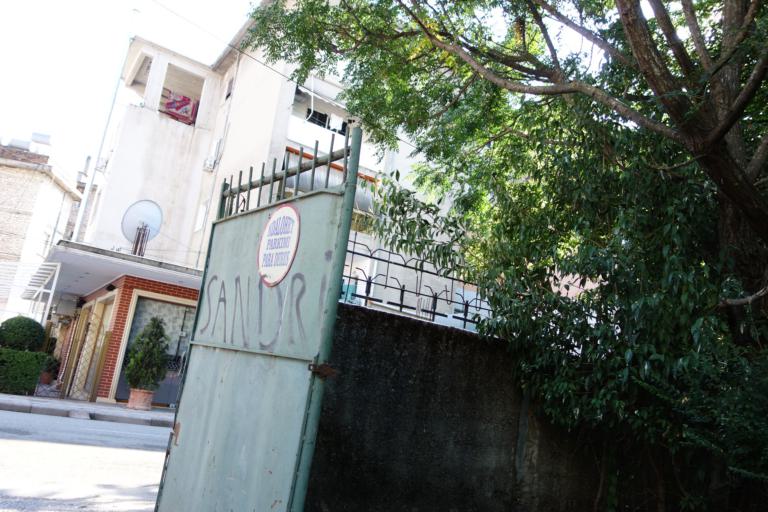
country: AL
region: Gjirokaster
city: Gjirokaster
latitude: 40.0813
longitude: 20.1423
